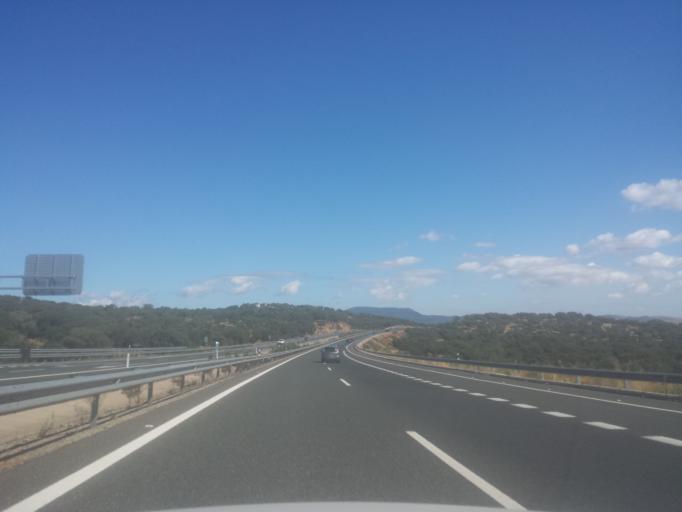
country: ES
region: Andalusia
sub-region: Provincia de Huelva
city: Santa Olalla del Cala
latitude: 37.9219
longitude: -6.2261
